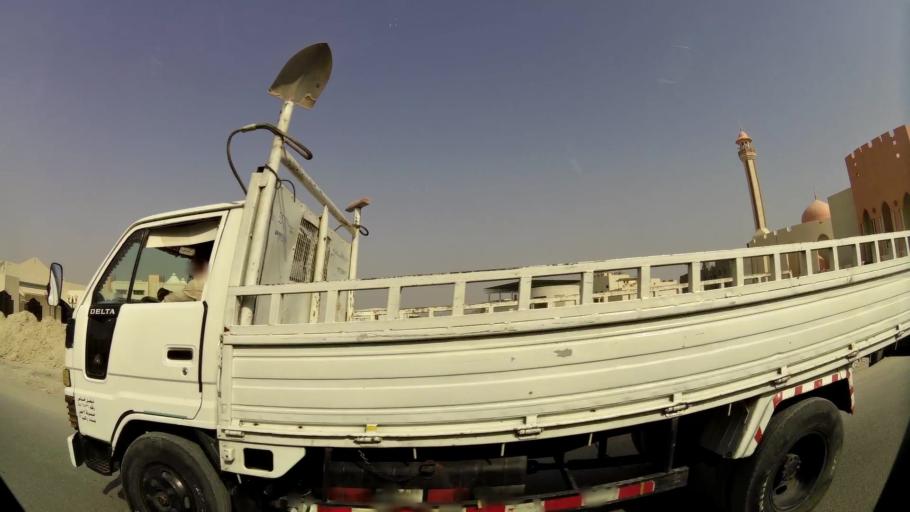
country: KW
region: Muhafazat al Jahra'
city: Al Jahra'
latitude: 29.3534
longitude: 47.7467
